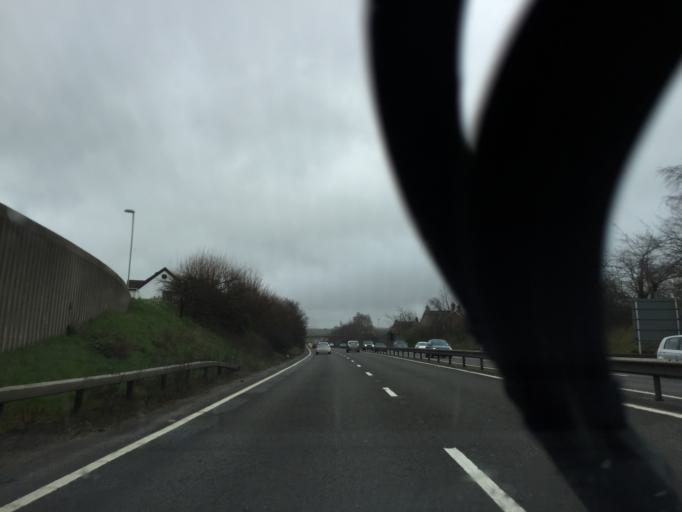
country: GB
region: England
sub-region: Hampshire
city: Ringwood
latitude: 50.8497
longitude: -1.7837
